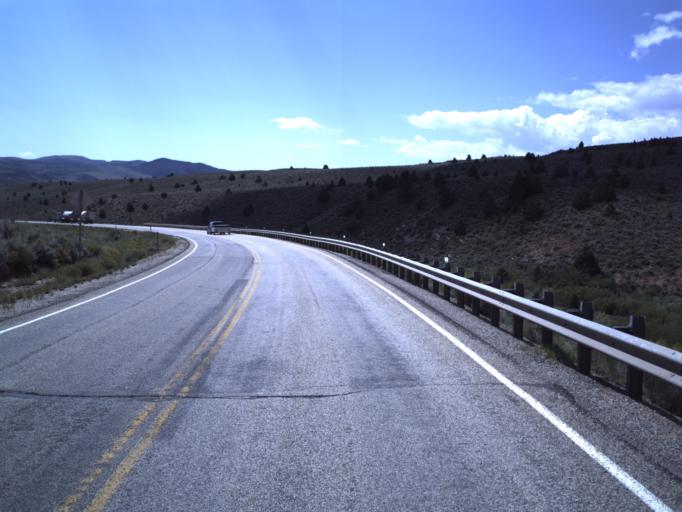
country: US
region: Utah
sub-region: Carbon County
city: Helper
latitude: 39.8296
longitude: -110.7882
